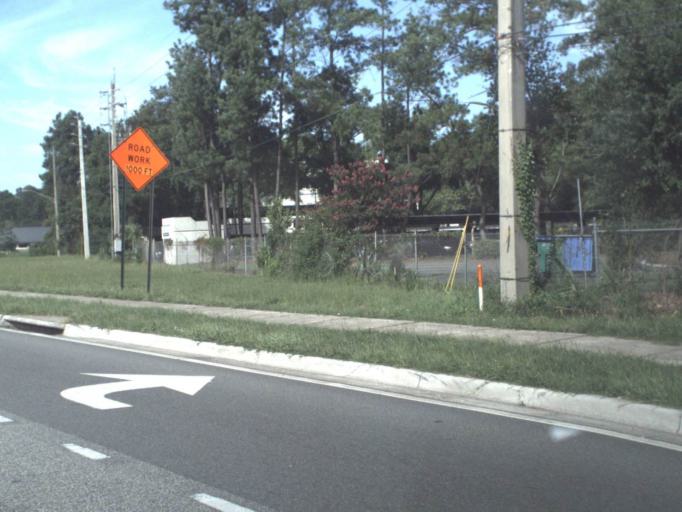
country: US
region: Florida
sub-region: Saint Johns County
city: Fruit Cove
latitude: 30.1850
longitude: -81.6286
